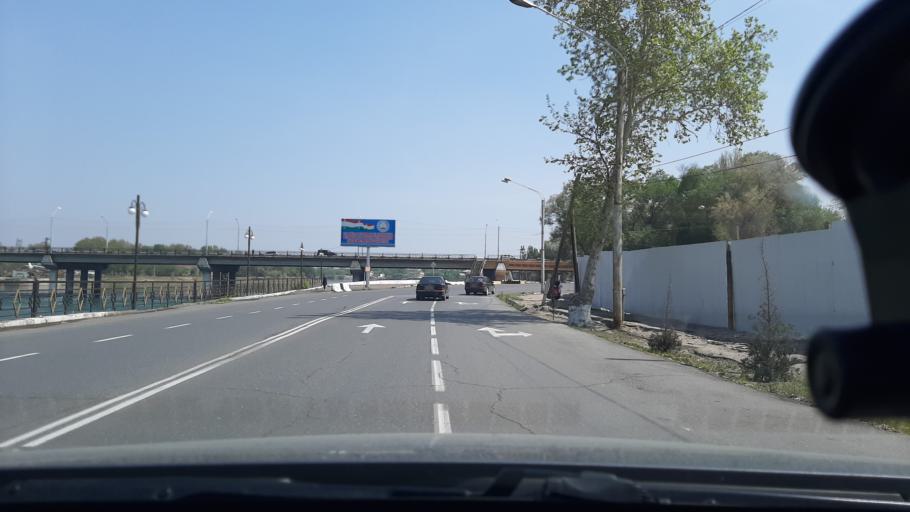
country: TJ
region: Viloyati Sughd
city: Khujand
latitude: 40.2929
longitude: 69.6381
